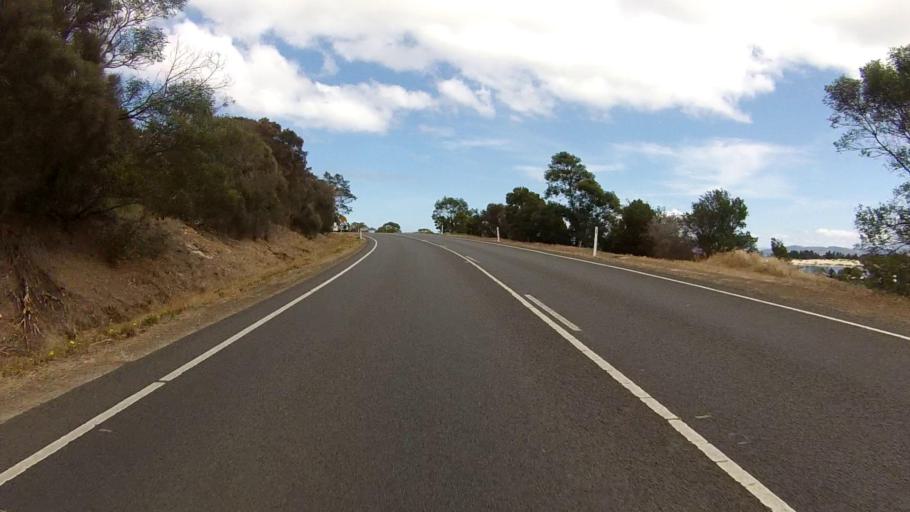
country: AU
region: Tasmania
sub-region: Sorell
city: Sorell
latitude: -42.8372
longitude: 147.6233
